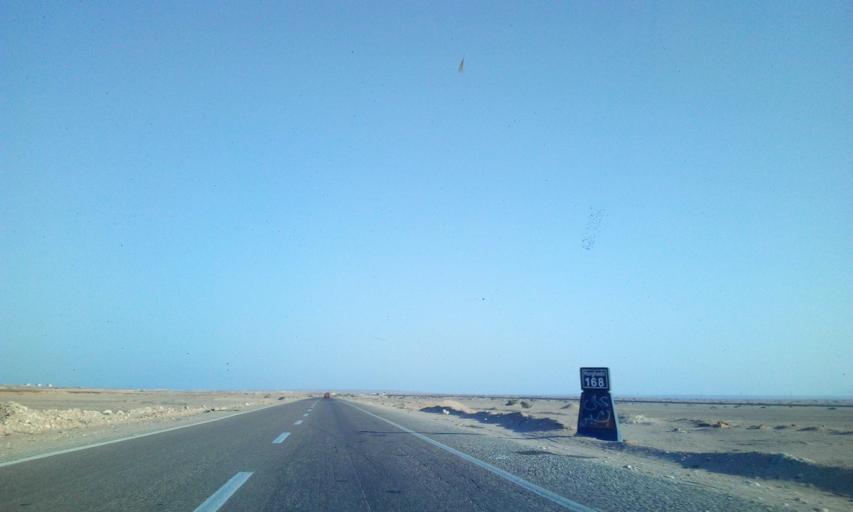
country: EG
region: South Sinai
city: Tor
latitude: 28.4598
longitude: 32.9884
